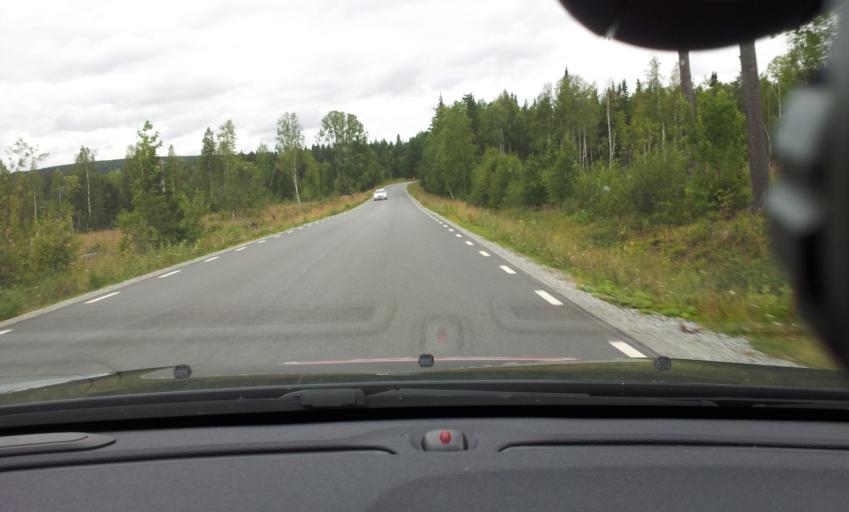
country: SE
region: Jaemtland
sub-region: Braecke Kommun
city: Braecke
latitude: 63.0825
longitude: 15.4119
